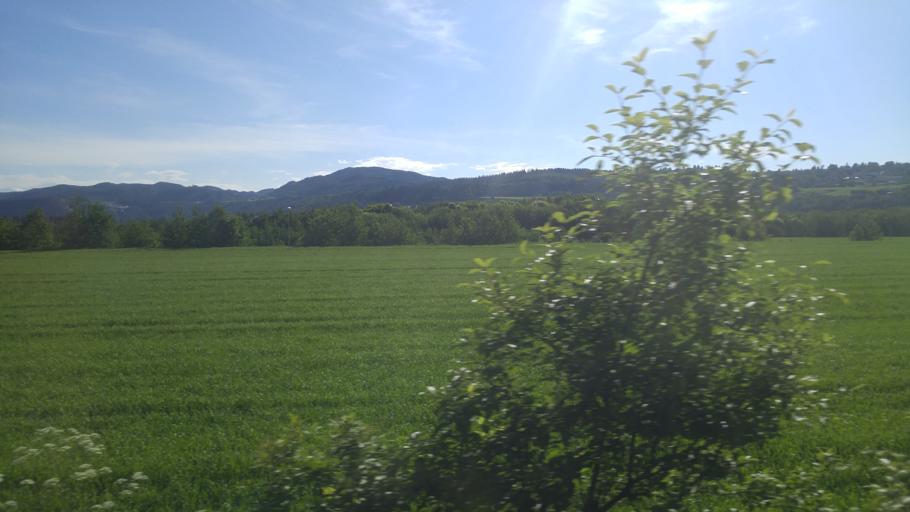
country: NO
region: Sor-Trondelag
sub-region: Melhus
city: Melhus
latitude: 63.2773
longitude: 10.2861
